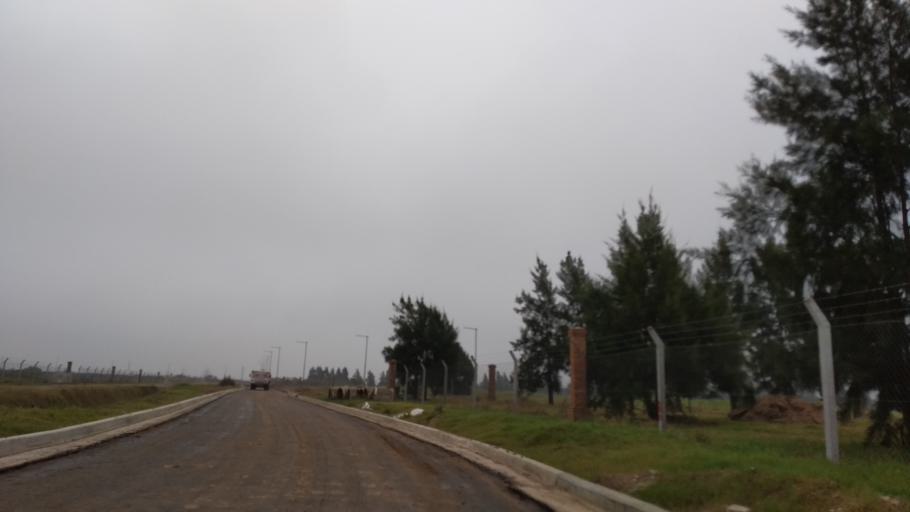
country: AR
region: Santa Fe
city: Funes
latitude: -32.9425
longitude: -60.7694
